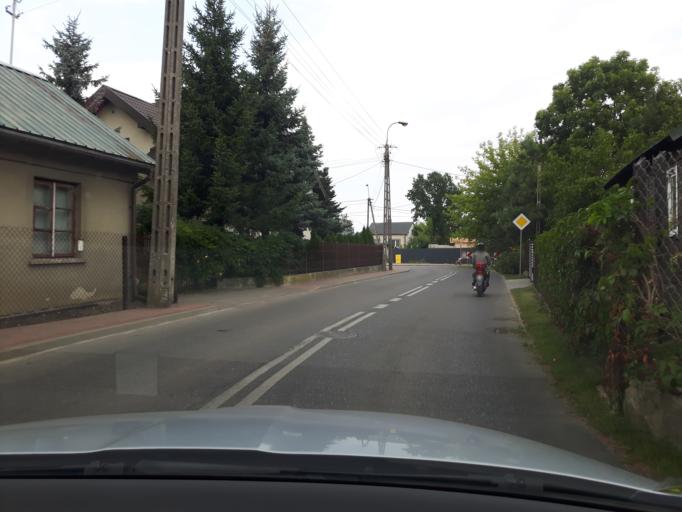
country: PL
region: Masovian Voivodeship
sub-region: Powiat legionowski
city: Wieliszew
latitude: 52.4559
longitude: 20.9600
